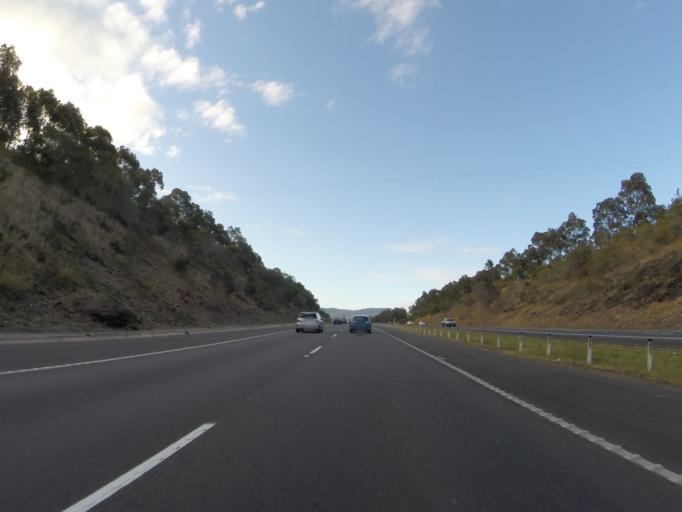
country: AU
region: New South Wales
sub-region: Wollongong
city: Dapto
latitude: -34.5194
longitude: 150.7889
